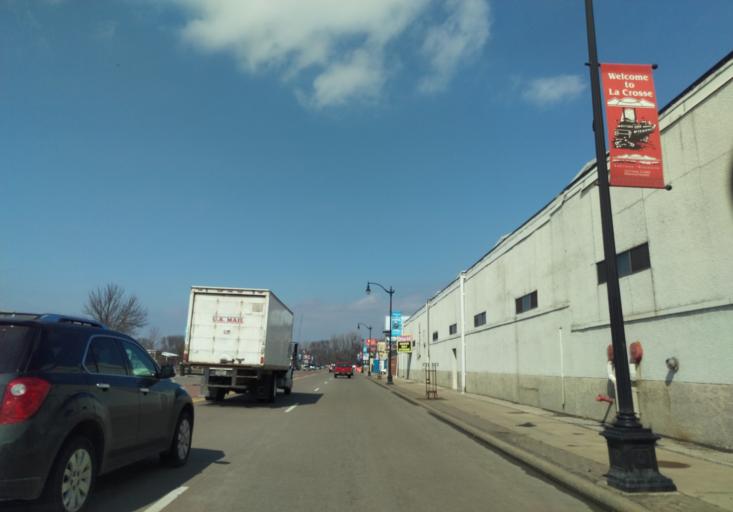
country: US
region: Wisconsin
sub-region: La Crosse County
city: North La Crosse
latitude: 43.8483
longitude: -91.2481
